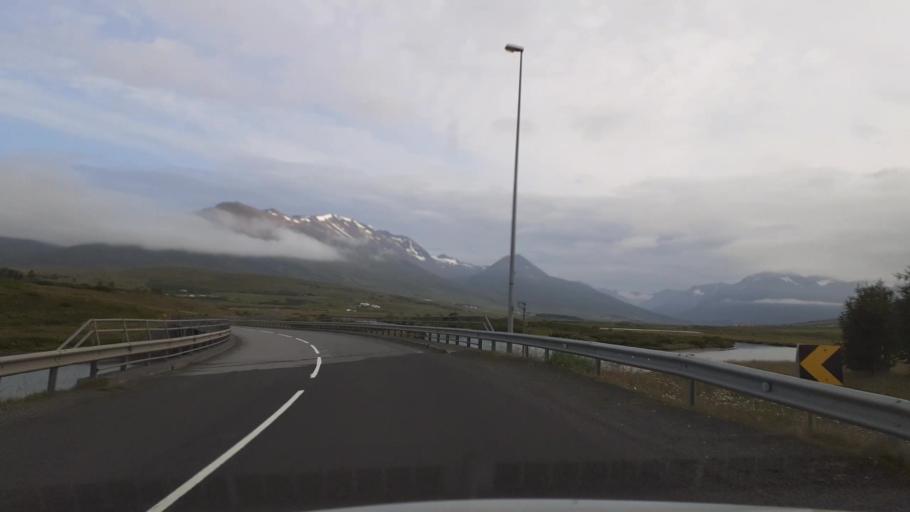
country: IS
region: Northeast
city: Dalvik
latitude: 65.9607
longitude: -18.5391
